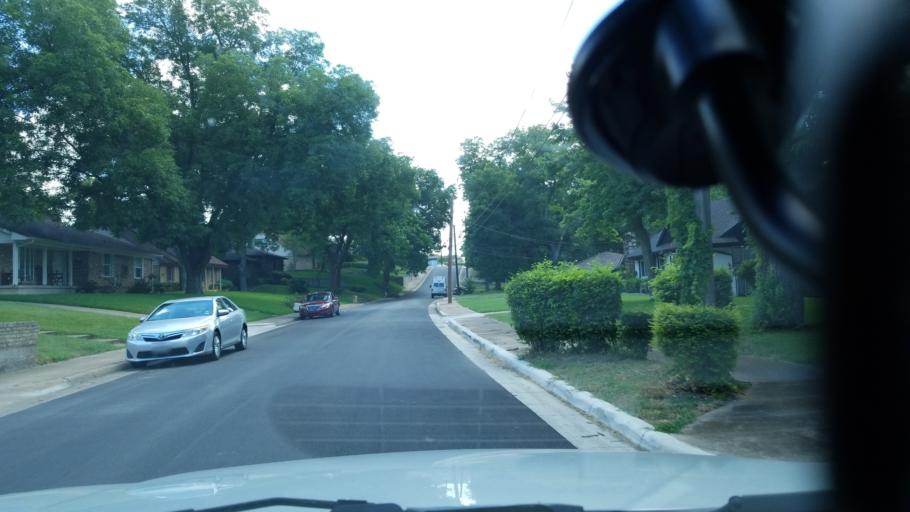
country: US
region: Texas
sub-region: Dallas County
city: Duncanville
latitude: 32.6673
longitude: -96.8608
